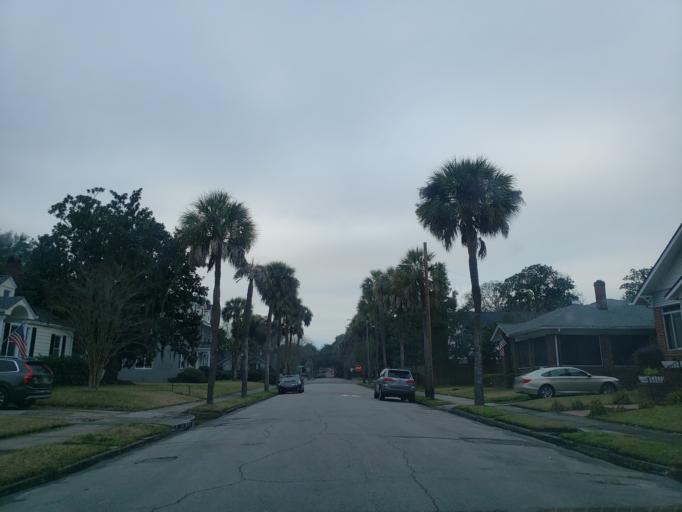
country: US
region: Georgia
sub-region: Chatham County
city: Savannah
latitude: 32.0434
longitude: -81.1015
